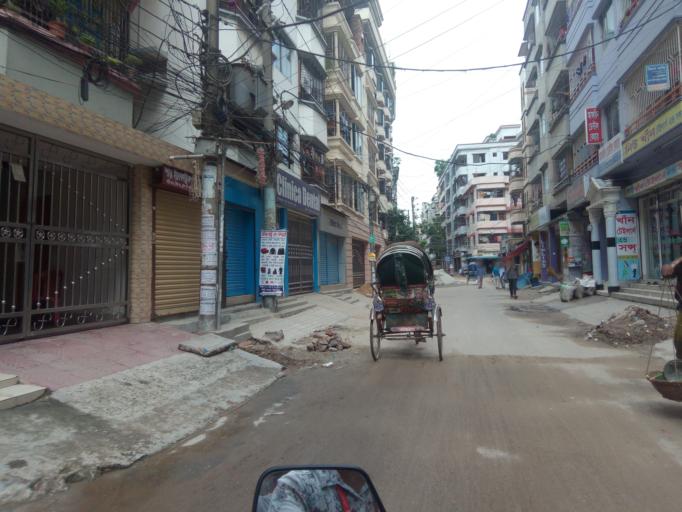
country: BD
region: Dhaka
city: Paltan
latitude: 23.7631
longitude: 90.4277
